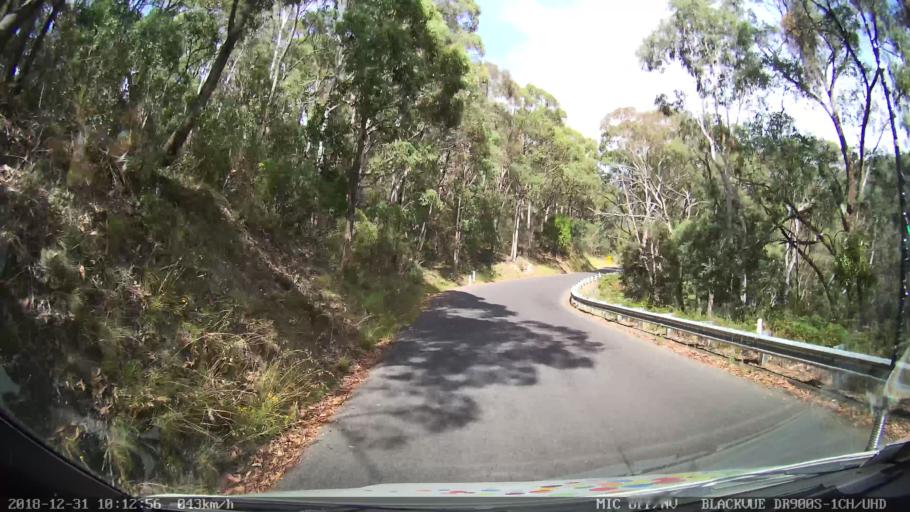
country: AU
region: New South Wales
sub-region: Snowy River
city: Jindabyne
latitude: -36.5377
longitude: 148.1589
